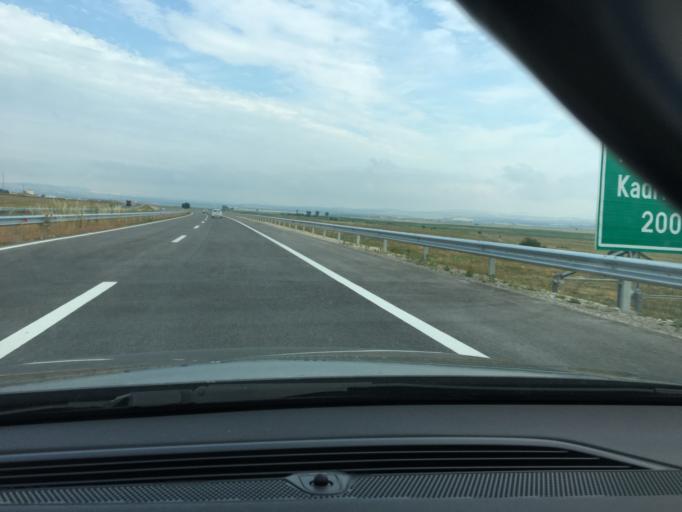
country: MK
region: Sveti Nikole
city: Sveti Nikole
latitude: 41.8056
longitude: 22.0679
